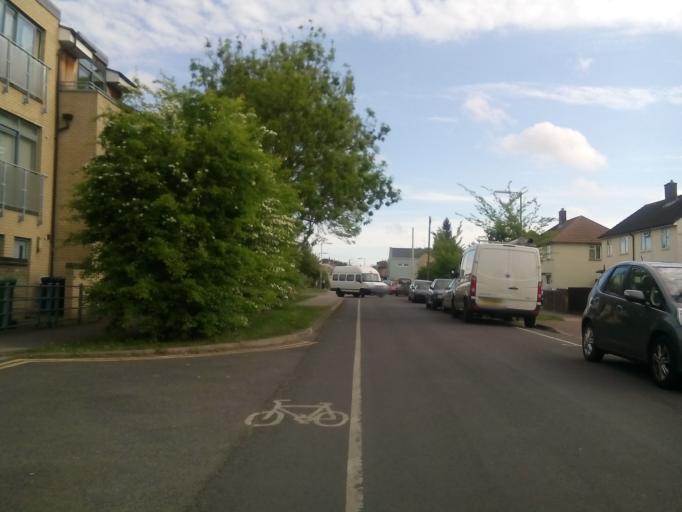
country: GB
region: England
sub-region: Cambridgeshire
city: Cambridge
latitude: 52.1946
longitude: 0.1417
